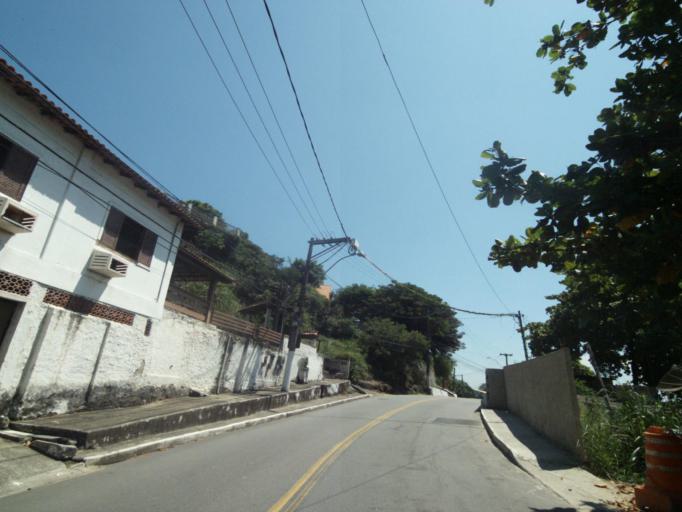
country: BR
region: Rio de Janeiro
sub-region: Niteroi
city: Niteroi
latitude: -22.9311
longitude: -43.1172
